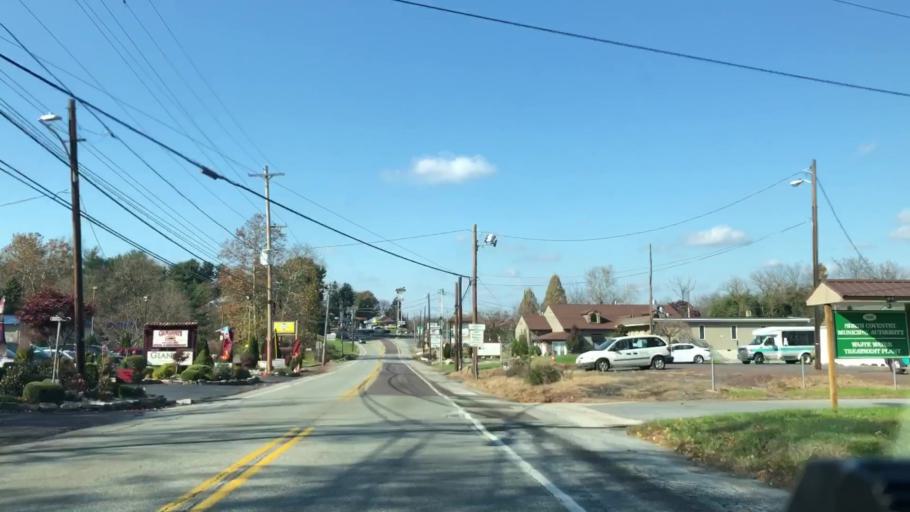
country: US
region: Pennsylvania
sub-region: Chester County
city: Kenilworth
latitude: 40.2283
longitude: -75.6248
